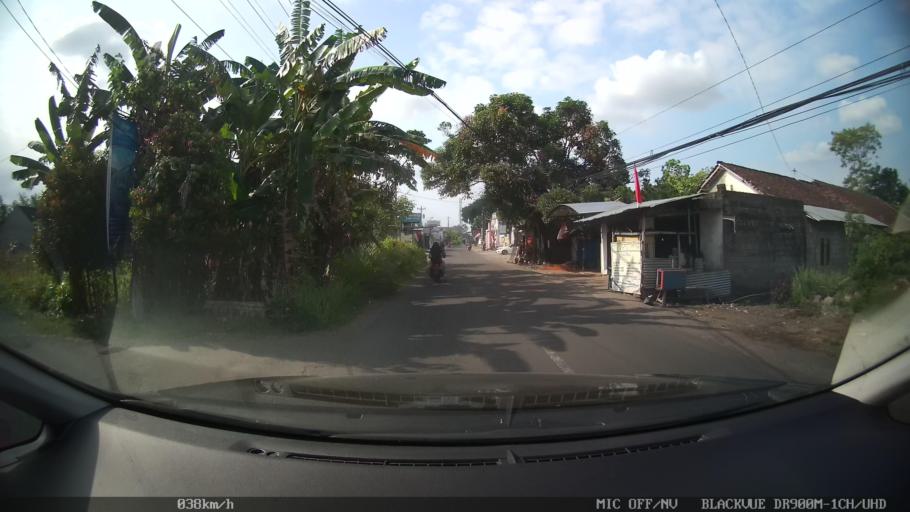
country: ID
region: Daerah Istimewa Yogyakarta
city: Depok
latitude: -7.7418
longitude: 110.4512
